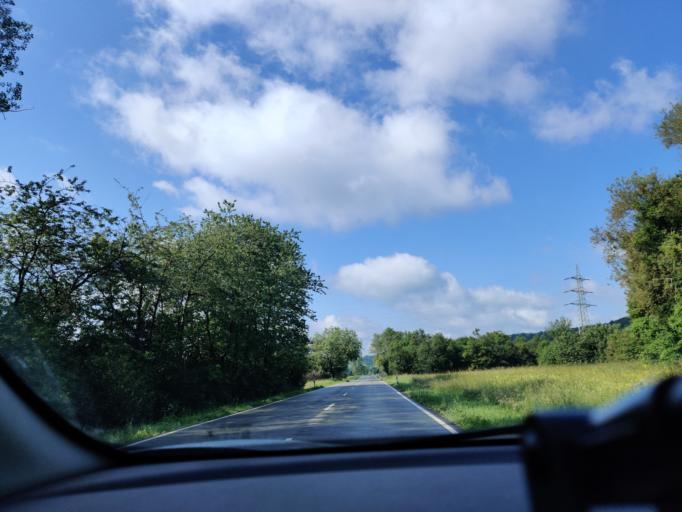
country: DE
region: Saarland
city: Gersheim
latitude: 49.1953
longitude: 7.1682
